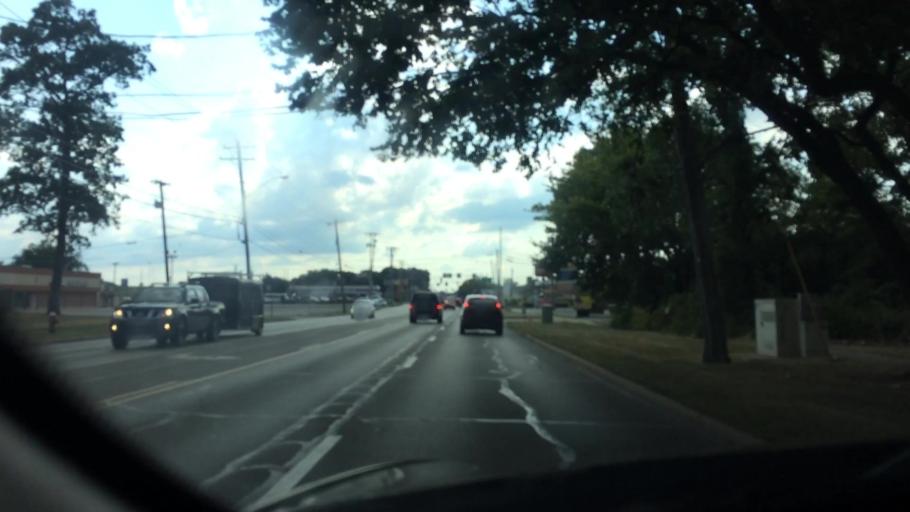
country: US
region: Ohio
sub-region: Lucas County
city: Maumee
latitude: 41.5947
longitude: -83.6616
